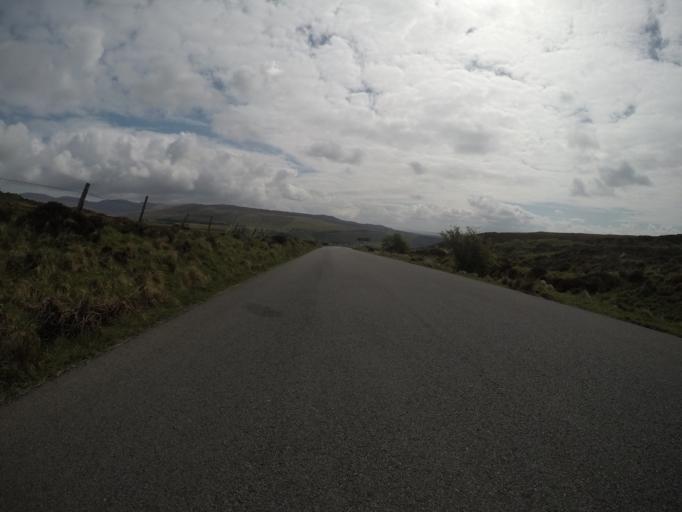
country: GB
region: Scotland
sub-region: Highland
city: Portree
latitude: 57.5947
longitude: -6.3735
